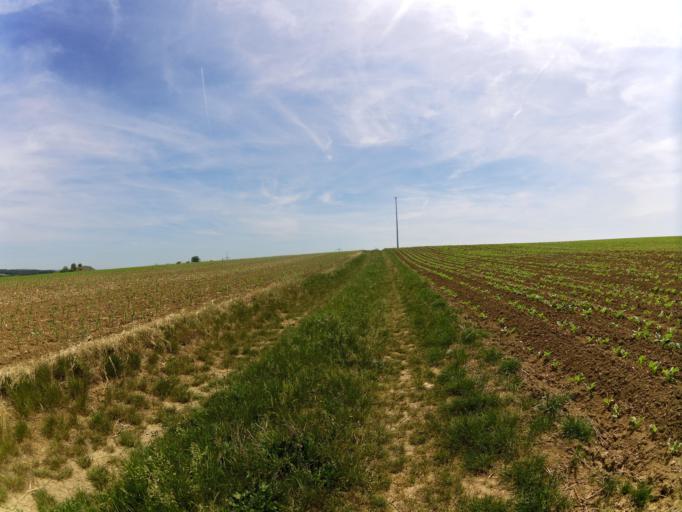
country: DE
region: Bavaria
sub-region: Regierungsbezirk Unterfranken
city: Sommerhausen
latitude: 49.6723
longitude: 10.0251
